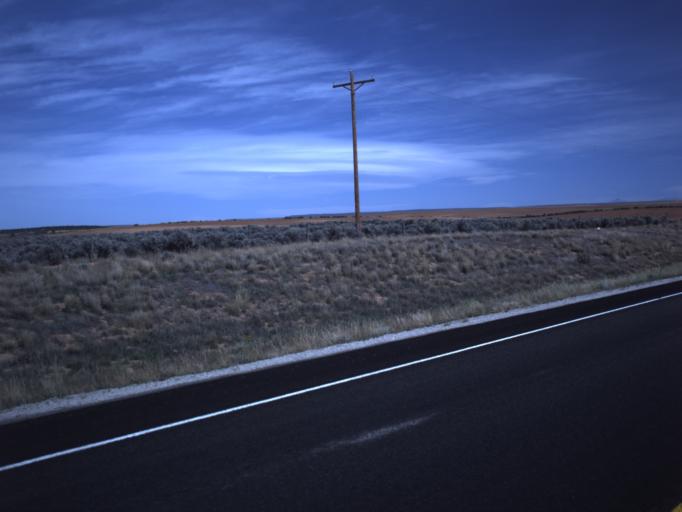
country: US
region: Utah
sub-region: San Juan County
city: Monticello
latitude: 37.8449
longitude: -109.1421
